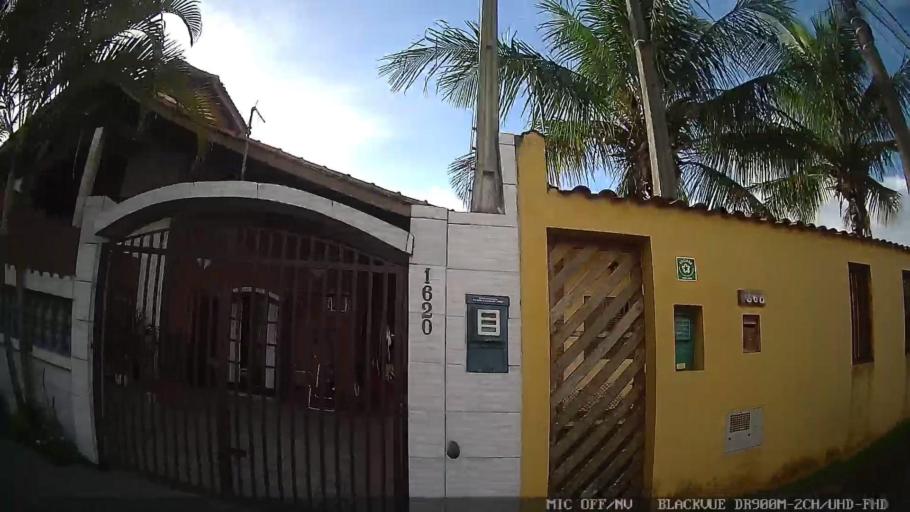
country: BR
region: Sao Paulo
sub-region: Itanhaem
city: Itanhaem
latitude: -24.2100
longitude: -46.8399
